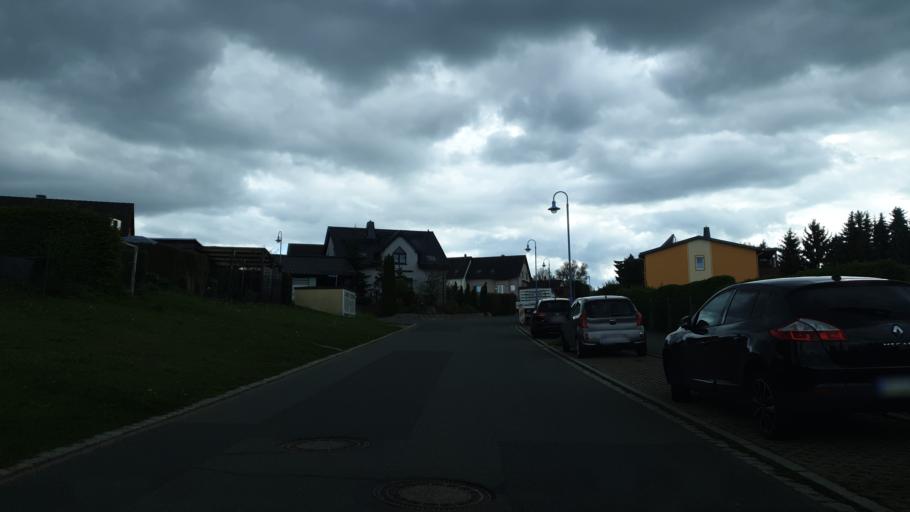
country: DE
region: Saxony
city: Oelsnitz
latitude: 50.7226
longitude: 12.7054
